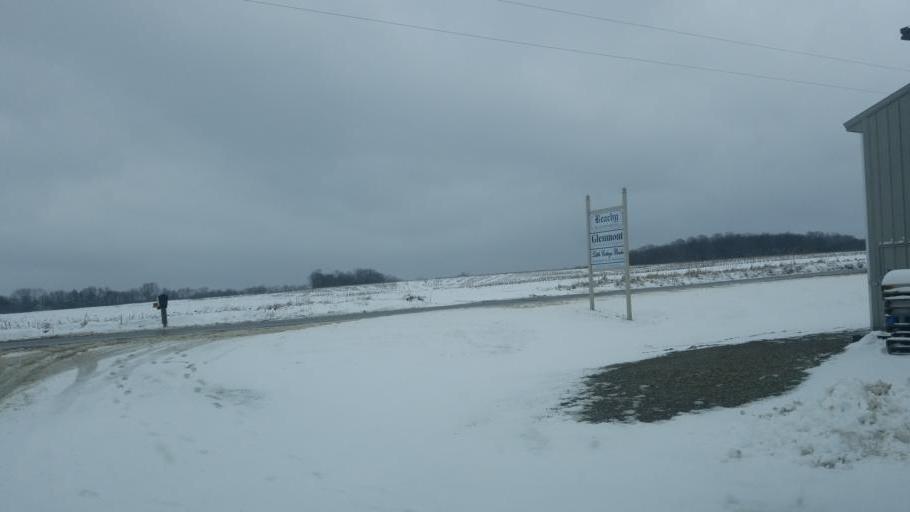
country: US
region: Ohio
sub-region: Knox County
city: Oak Hill
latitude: 40.4917
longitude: -82.1409
